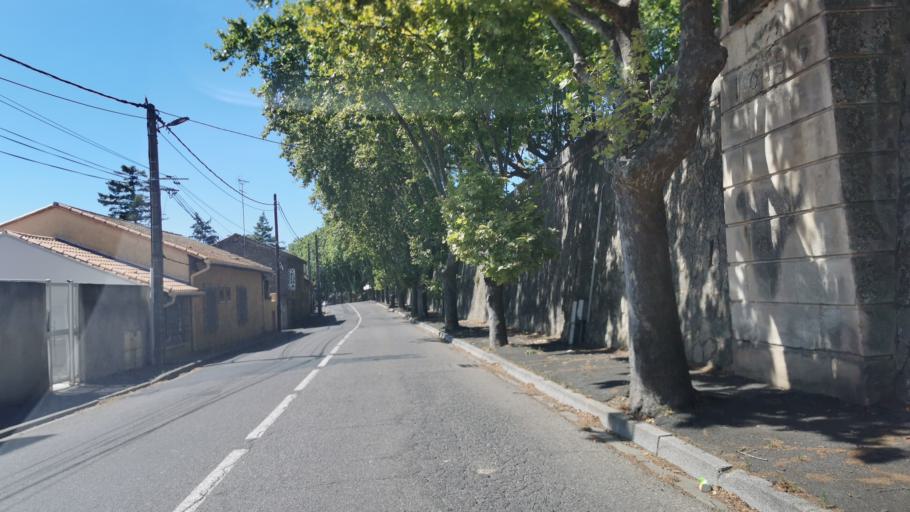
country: FR
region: Languedoc-Roussillon
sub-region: Departement de l'Herault
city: Beziers
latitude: 43.3575
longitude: 3.2122
